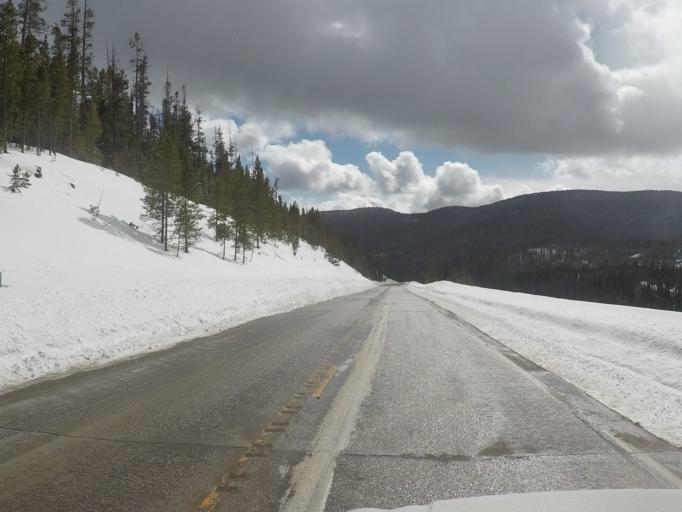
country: US
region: Montana
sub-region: Meagher County
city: White Sulphur Springs
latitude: 46.8216
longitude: -110.6997
